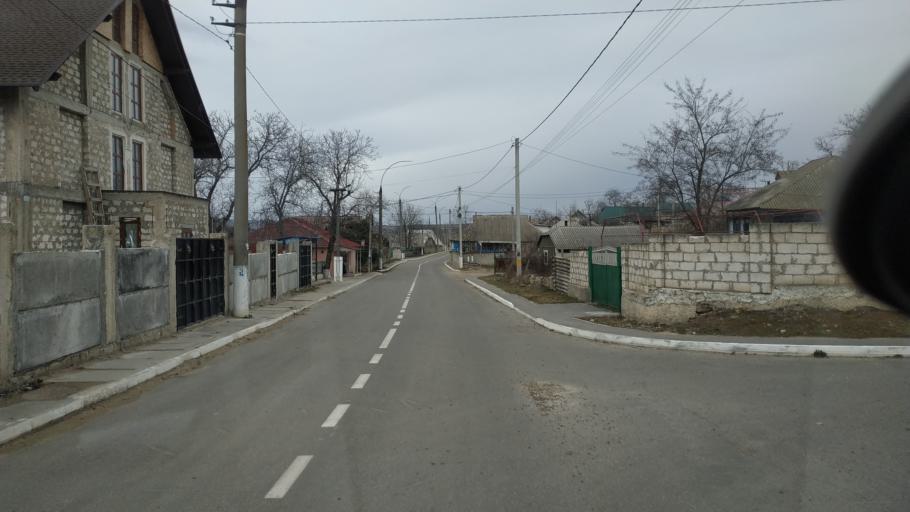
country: MD
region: Telenesti
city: Cocieri
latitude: 47.3476
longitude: 29.1105
